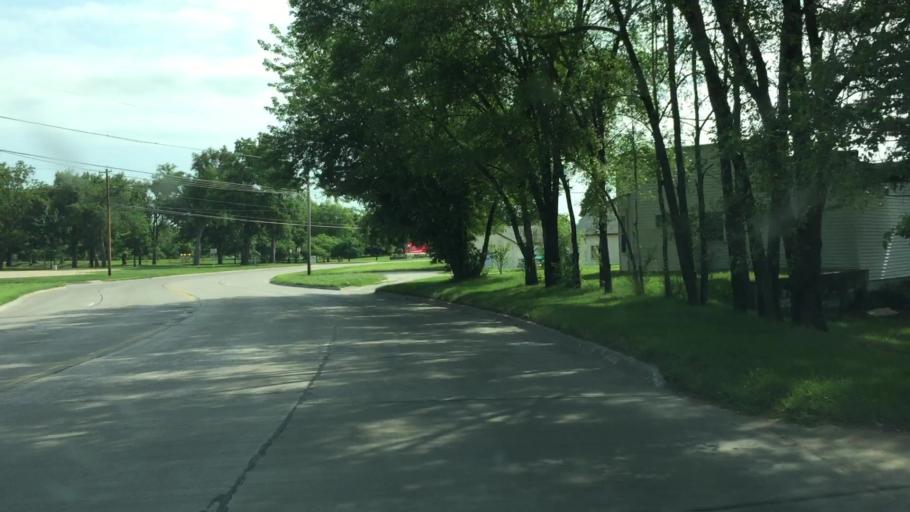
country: US
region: Iowa
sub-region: Lee County
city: Fort Madison
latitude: 40.6256
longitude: -91.3589
